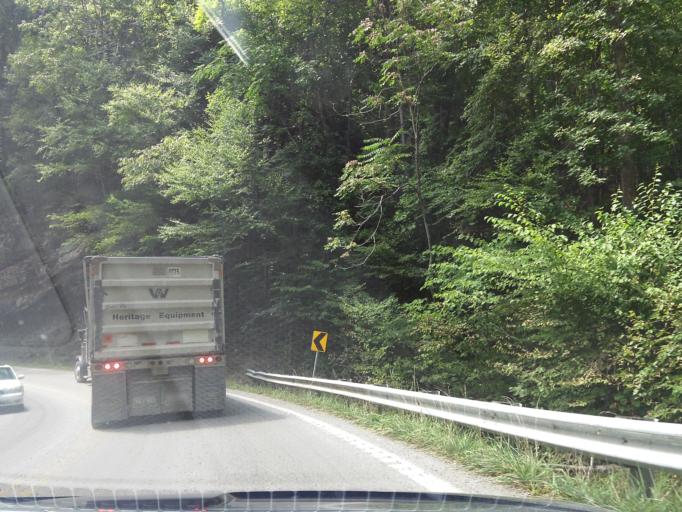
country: US
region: Kentucky
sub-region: Harlan County
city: Harlan
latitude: 36.8824
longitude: -83.3145
